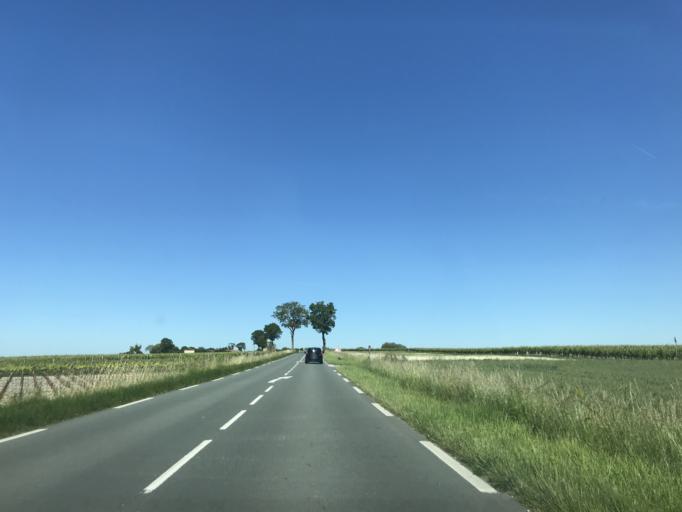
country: FR
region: Poitou-Charentes
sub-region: Departement de la Charente-Maritime
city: Perignac
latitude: 45.5767
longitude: -0.4346
